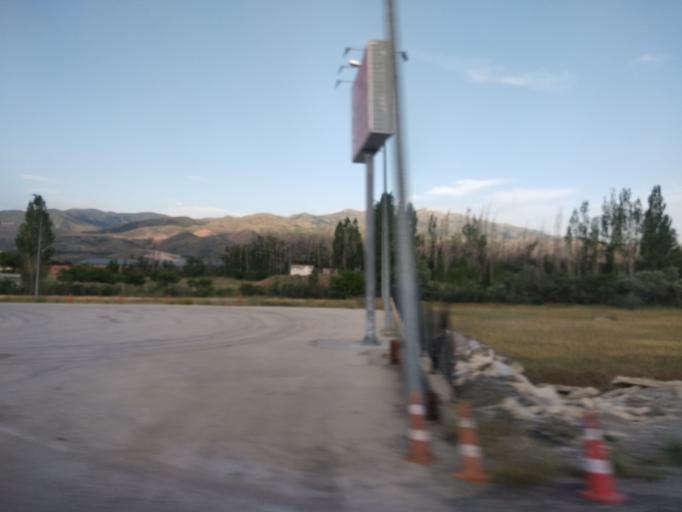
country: TR
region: Erzincan
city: Catalarmut
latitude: 39.8131
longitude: 39.3571
